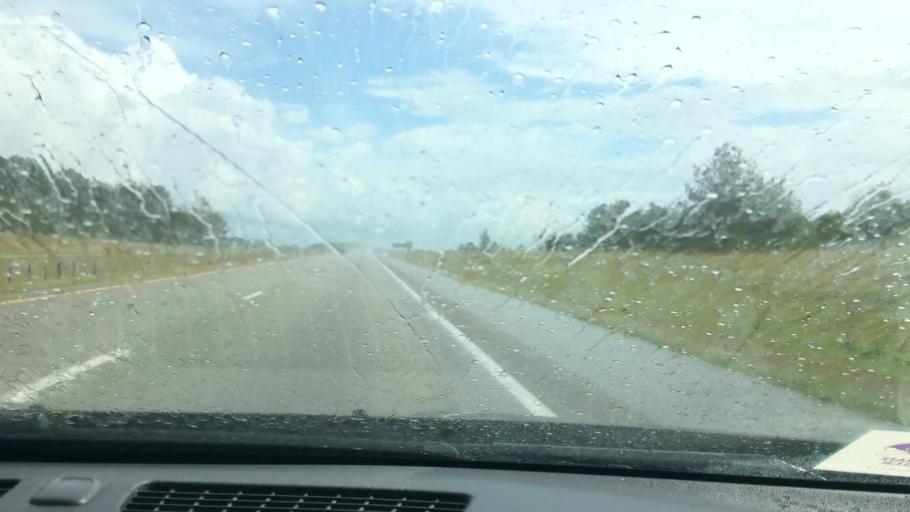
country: US
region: North Carolina
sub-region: Wilson County
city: Wilson
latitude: 35.6700
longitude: -77.8881
